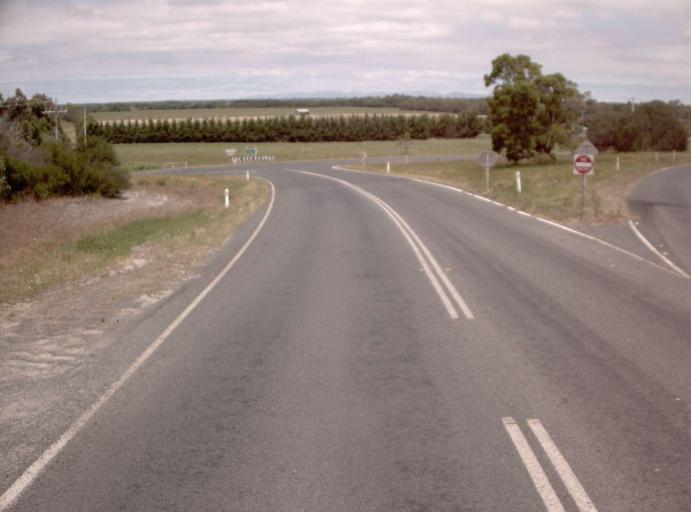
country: AU
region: Victoria
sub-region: Latrobe
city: Traralgon
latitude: -38.5455
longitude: 146.7013
